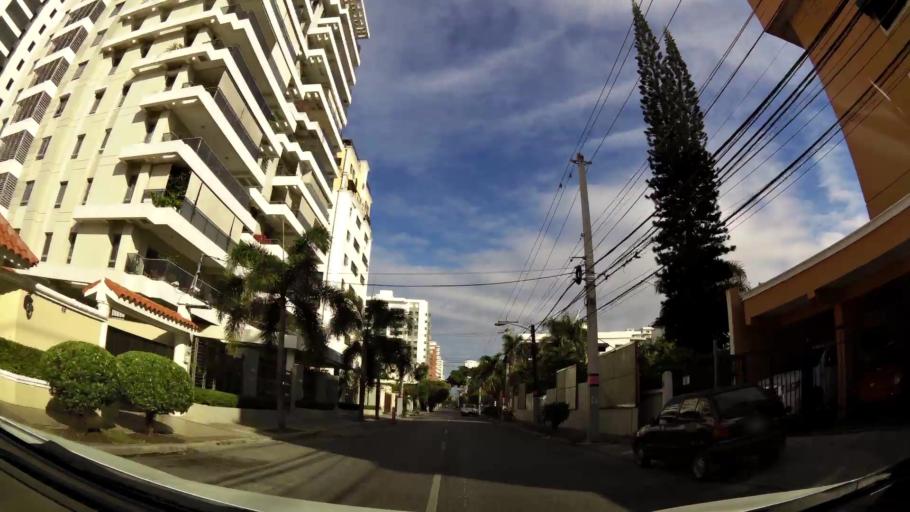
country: DO
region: Nacional
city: La Julia
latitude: 18.4743
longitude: -69.9378
